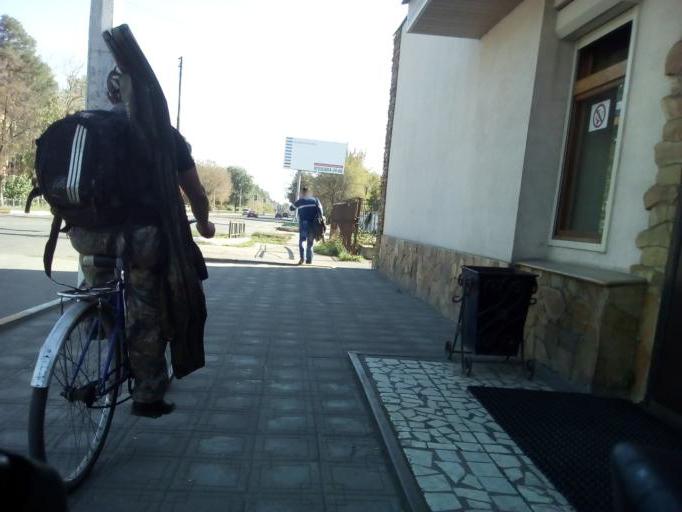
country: RU
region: Moskovskaya
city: Ramenskoye
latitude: 55.5613
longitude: 38.2477
